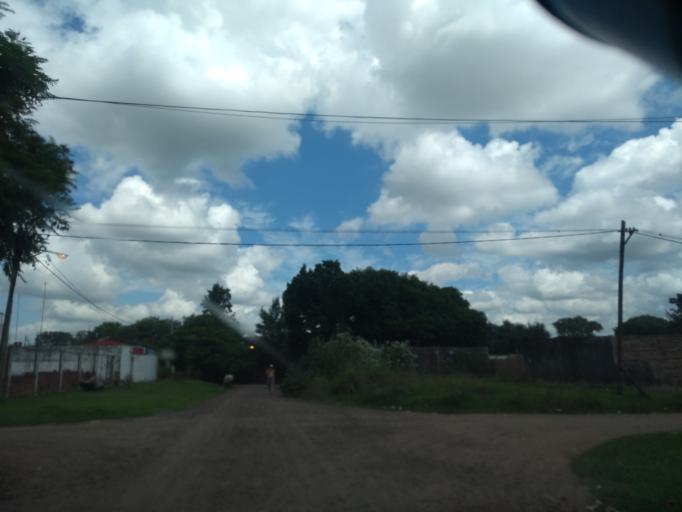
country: AR
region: Chaco
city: Fontana
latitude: -27.4100
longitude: -59.0452
